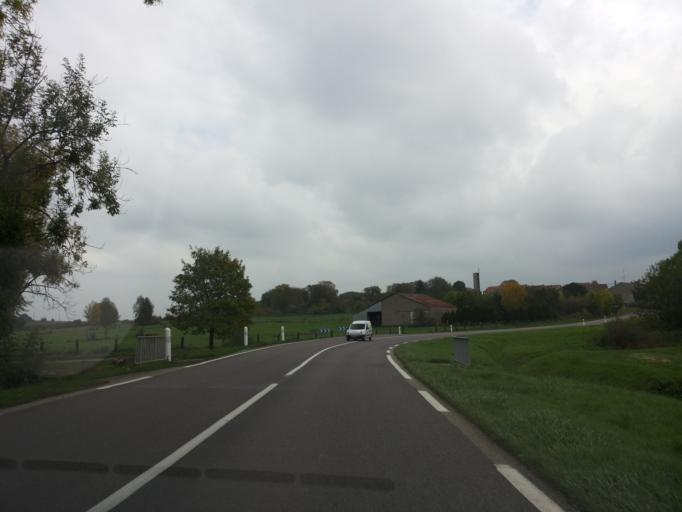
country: FR
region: Lorraine
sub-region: Departement de la Moselle
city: Dieuze
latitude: 48.7234
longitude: 6.7213
